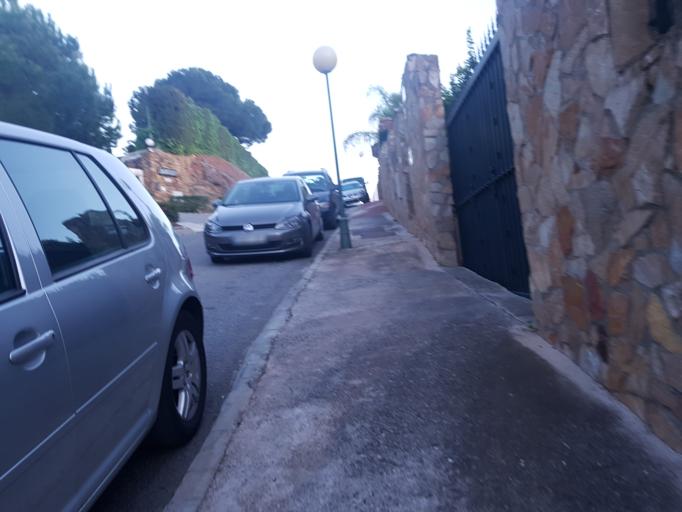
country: ES
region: Andalusia
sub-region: Provincia de Malaga
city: Marbella
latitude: 36.5221
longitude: -4.8879
